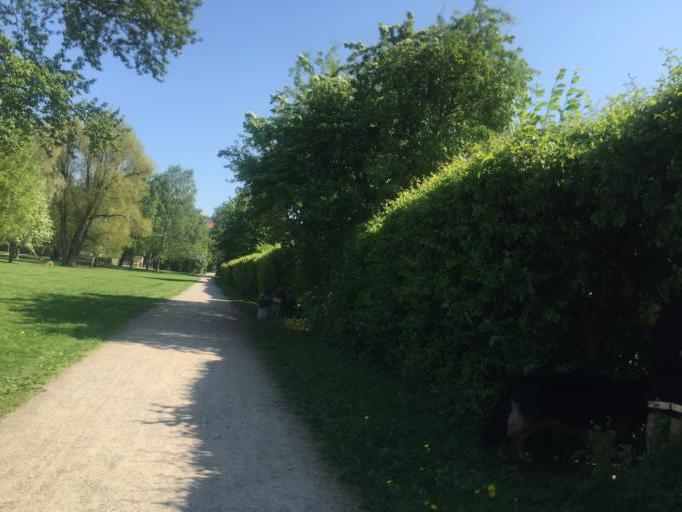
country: SE
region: Stockholm
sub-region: Stockholms Kommun
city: Arsta
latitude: 59.2839
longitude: 18.0645
